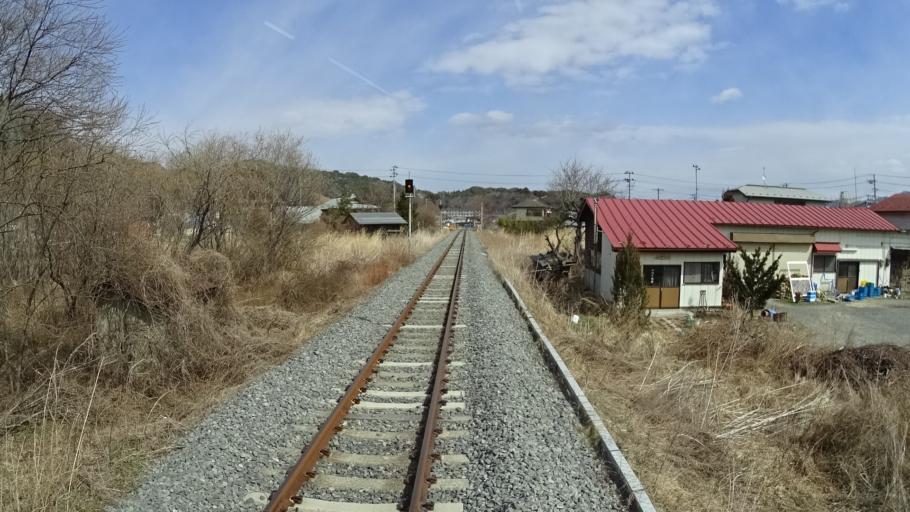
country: JP
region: Iwate
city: Miyako
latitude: 39.5757
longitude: 141.9344
